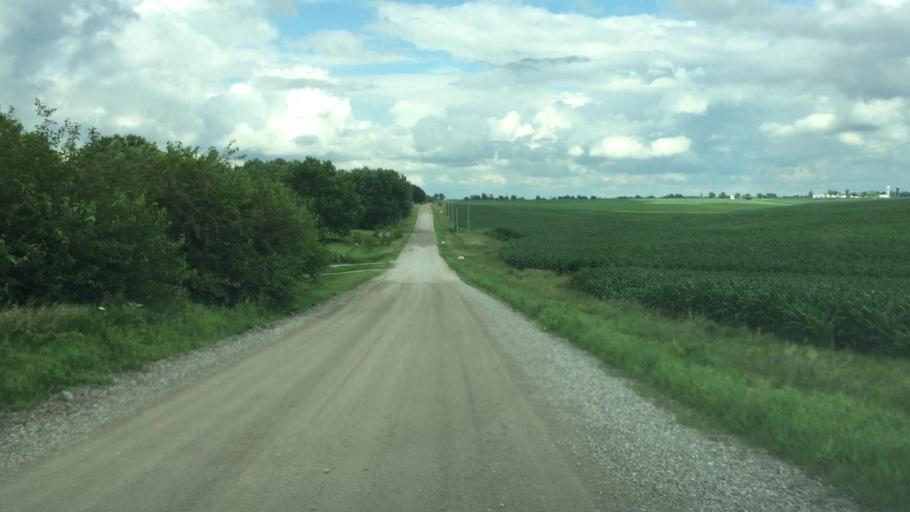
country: US
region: Iowa
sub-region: Jasper County
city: Newton
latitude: 41.7354
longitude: -93.0079
